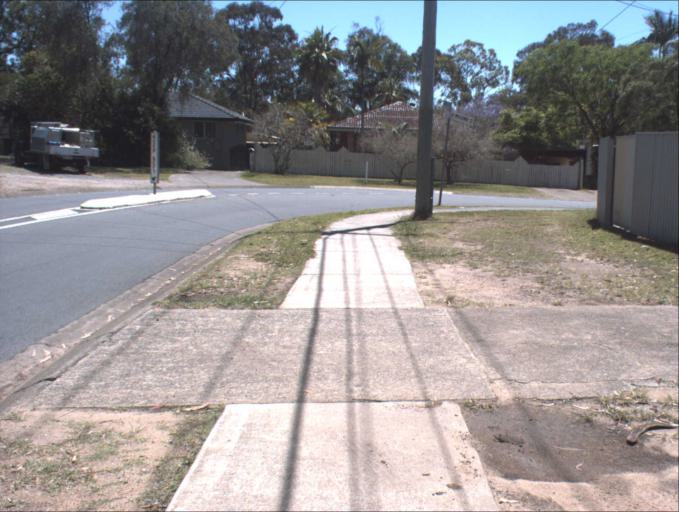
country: AU
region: Queensland
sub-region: Logan
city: Logan City
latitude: -27.6349
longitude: 153.1125
